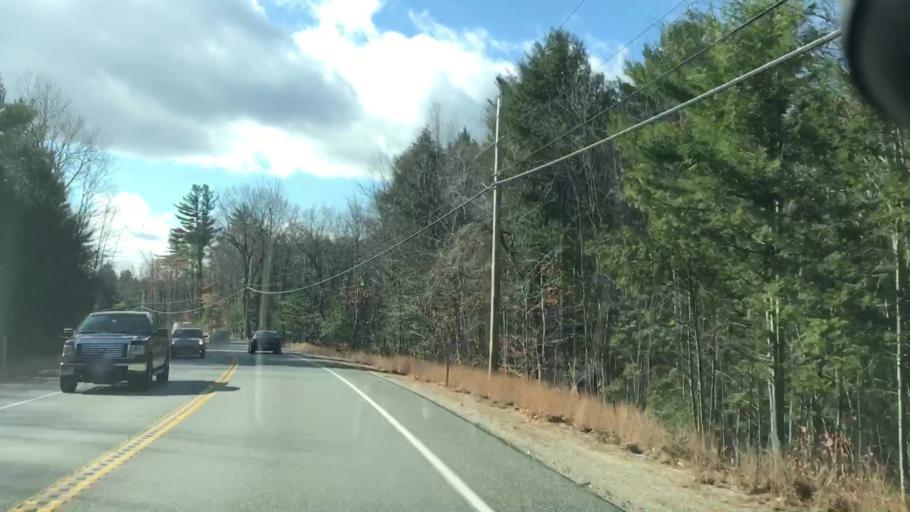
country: US
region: New Hampshire
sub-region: Carroll County
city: Ossipee
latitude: 43.6574
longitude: -71.1589
